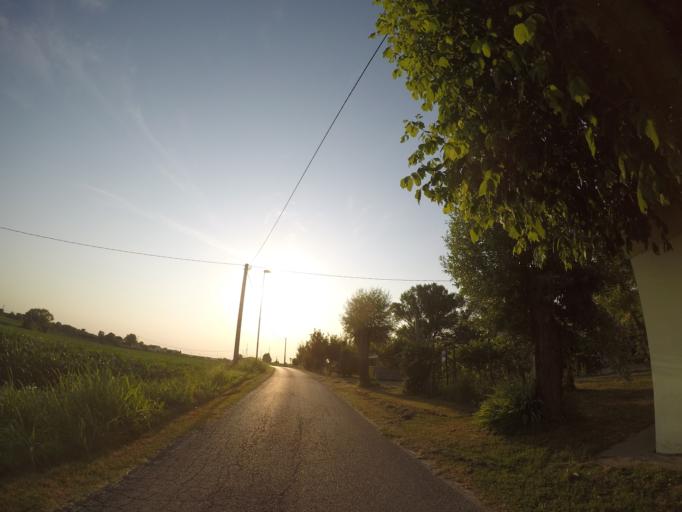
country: IT
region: Veneto
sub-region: Provincia di Rovigo
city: Fratta Polesine
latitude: 45.0044
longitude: 11.6449
